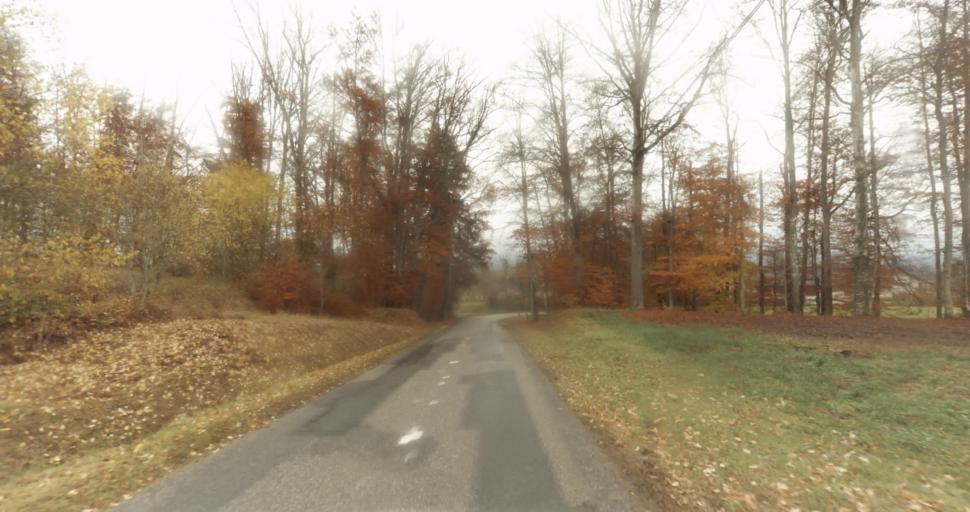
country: FR
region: Rhone-Alpes
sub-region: Departement de la Haute-Savoie
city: Evires
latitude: 46.0574
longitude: 6.2258
